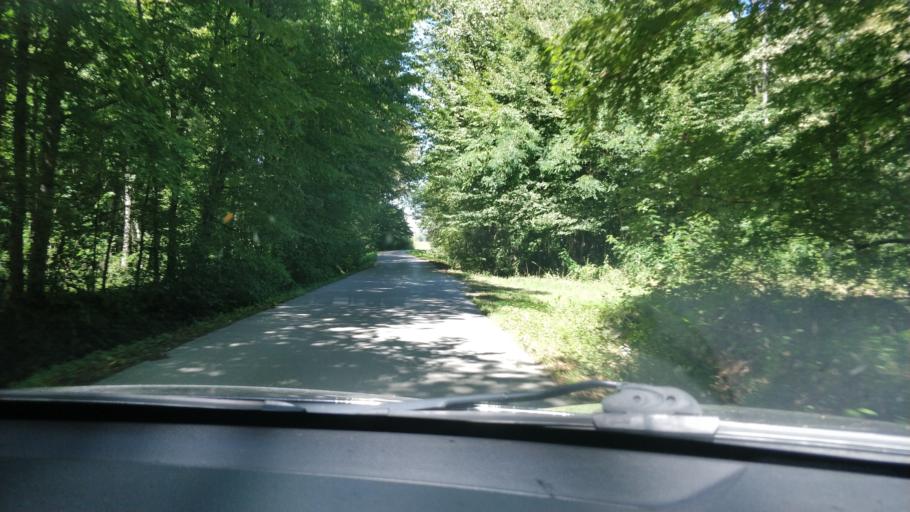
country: HR
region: Karlovacka
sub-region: Grad Karlovac
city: Karlovac
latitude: 45.4714
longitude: 15.6622
